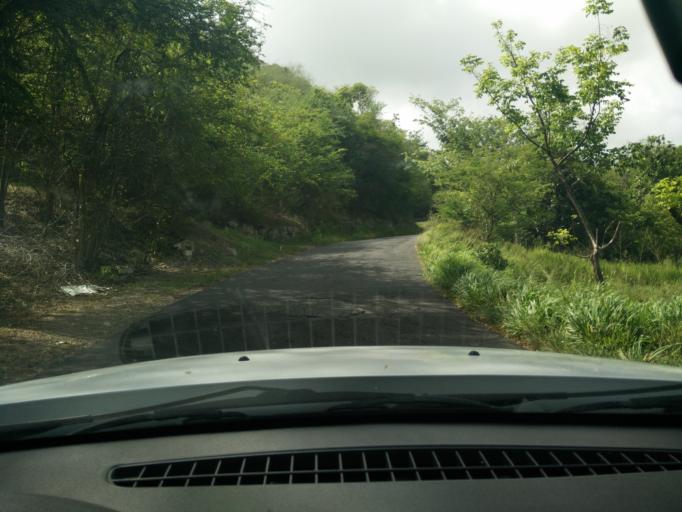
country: GP
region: Guadeloupe
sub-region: Guadeloupe
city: Le Gosier
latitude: 16.2292
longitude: -61.4572
